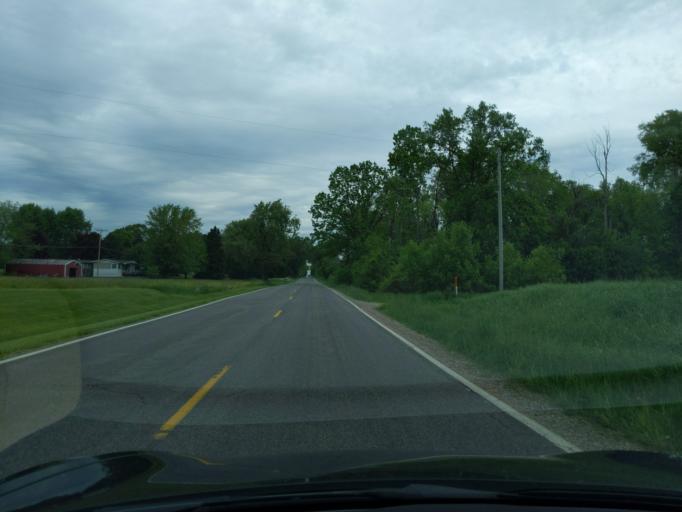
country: US
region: Michigan
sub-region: Ingham County
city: Mason
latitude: 42.5482
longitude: -84.3567
